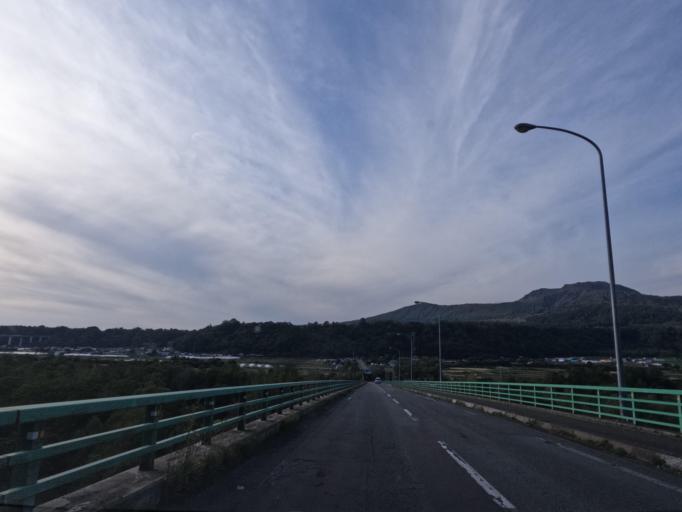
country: JP
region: Hokkaido
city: Date
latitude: 42.5068
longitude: 140.8649
